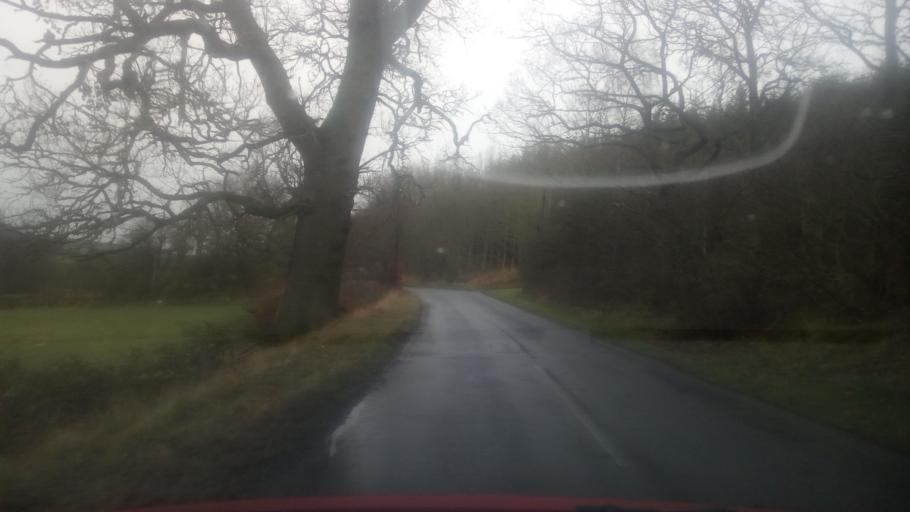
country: GB
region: Scotland
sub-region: The Scottish Borders
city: Earlston
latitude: 55.6202
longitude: -2.6651
